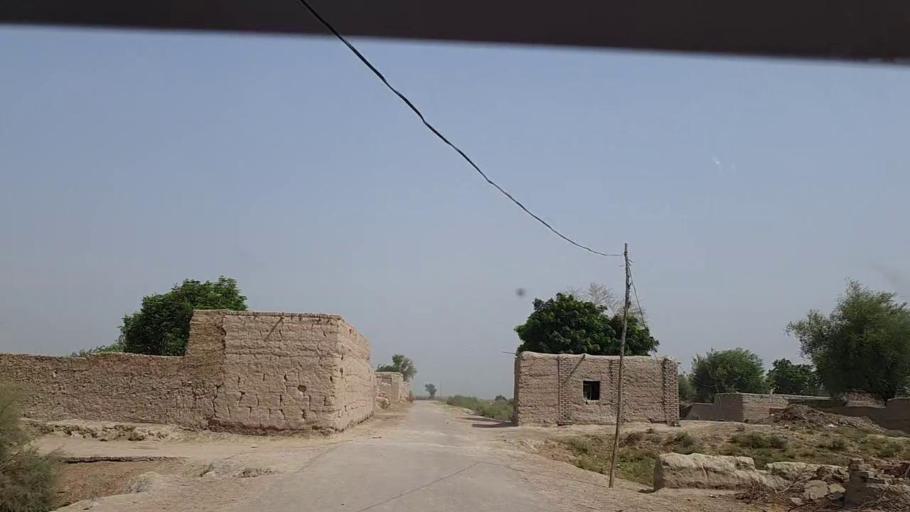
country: PK
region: Sindh
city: Khairpur Nathan Shah
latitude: 27.0464
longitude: 67.6845
